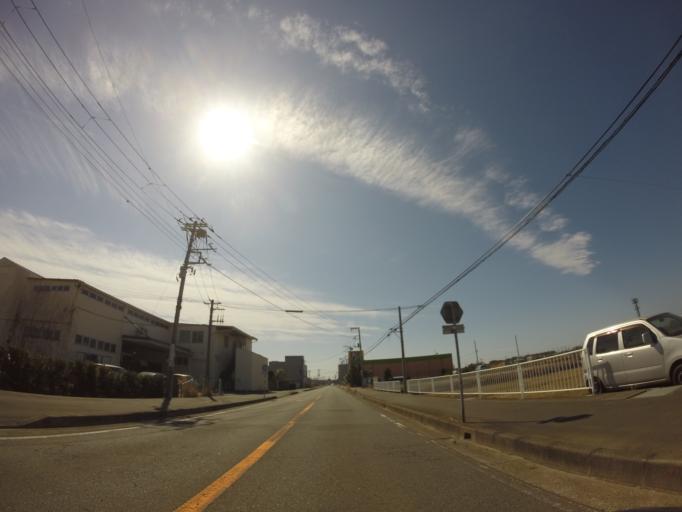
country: JP
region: Shizuoka
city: Numazu
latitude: 35.1248
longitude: 138.8236
